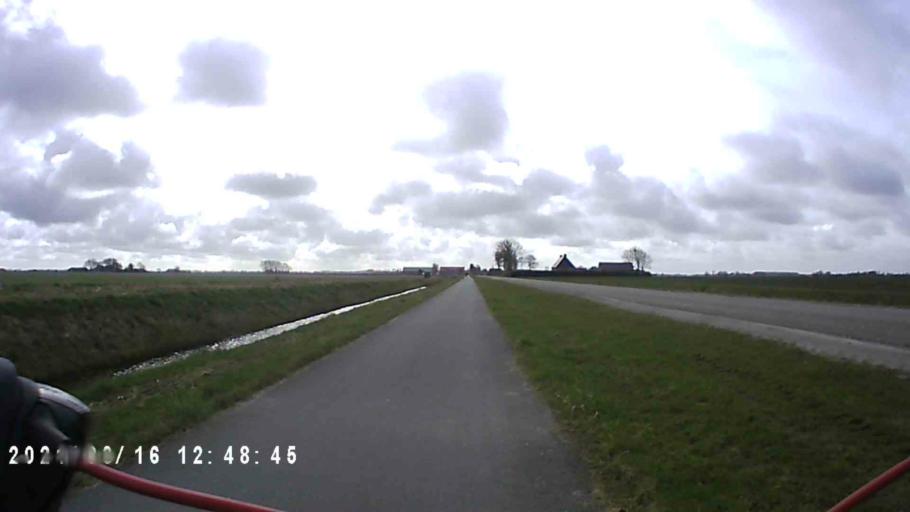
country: NL
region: Friesland
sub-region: Gemeente Het Bildt
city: Sint Annaparochie
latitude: 53.2702
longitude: 5.6775
